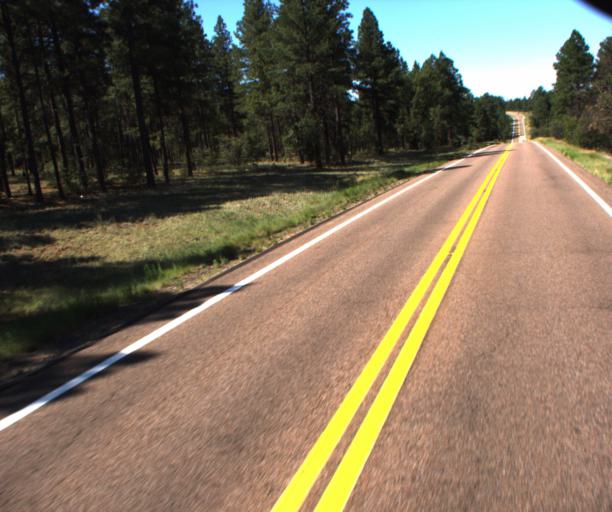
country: US
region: Arizona
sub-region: Navajo County
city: Lake of the Woods
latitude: 34.1022
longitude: -110.1613
